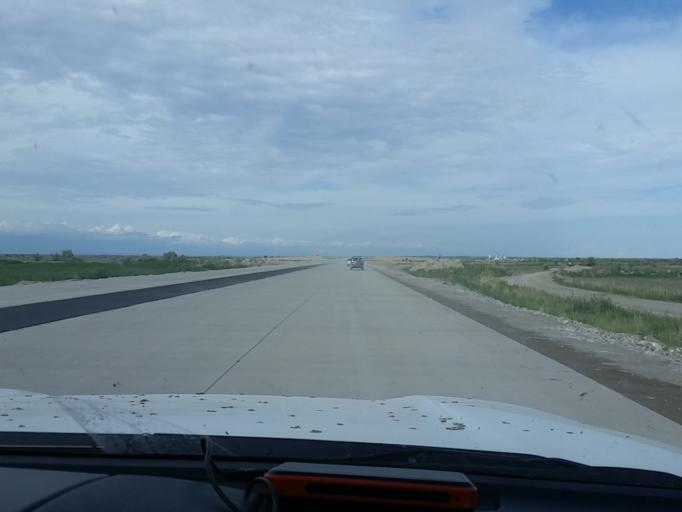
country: KZ
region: Almaty Oblysy
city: Zharkent
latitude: 44.0393
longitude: 79.9647
